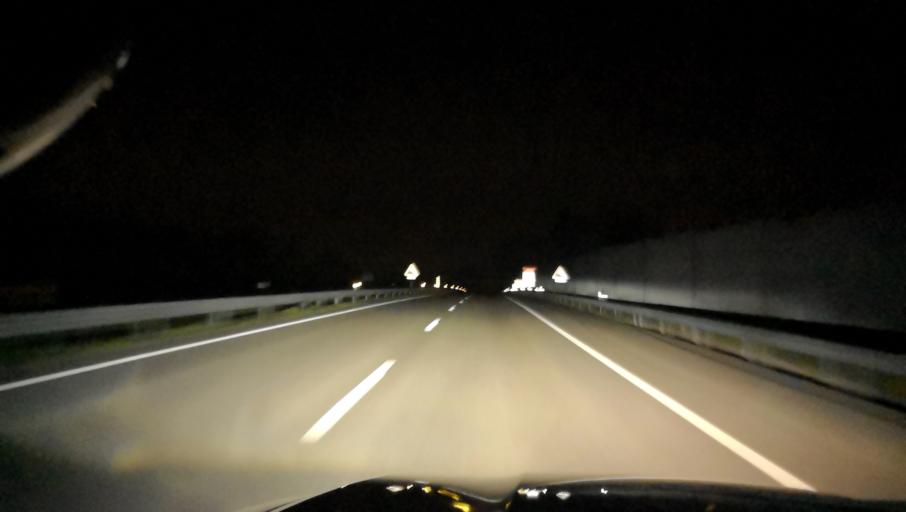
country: PT
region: Viseu
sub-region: Oliveira de Frades
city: Oliveira de Frades
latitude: 40.6817
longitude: -8.1828
